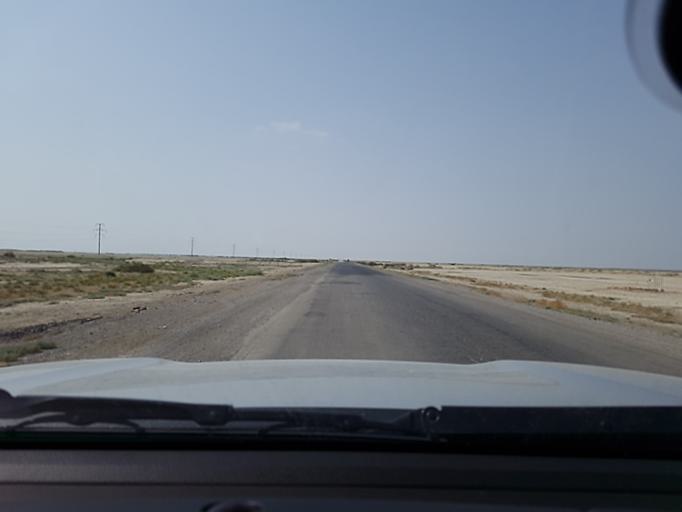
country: TM
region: Balkan
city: Gumdag
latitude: 38.9134
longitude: 54.5915
